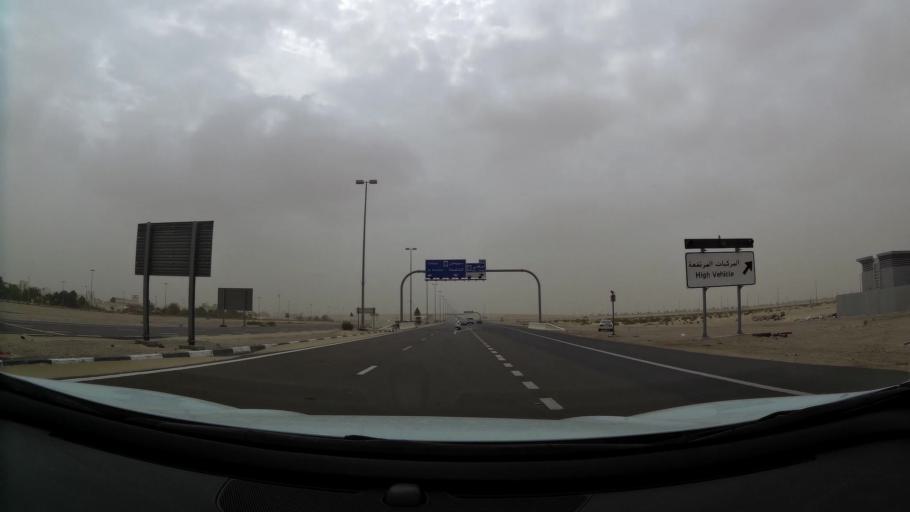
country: AE
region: Abu Dhabi
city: Abu Dhabi
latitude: 24.4243
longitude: 54.7129
